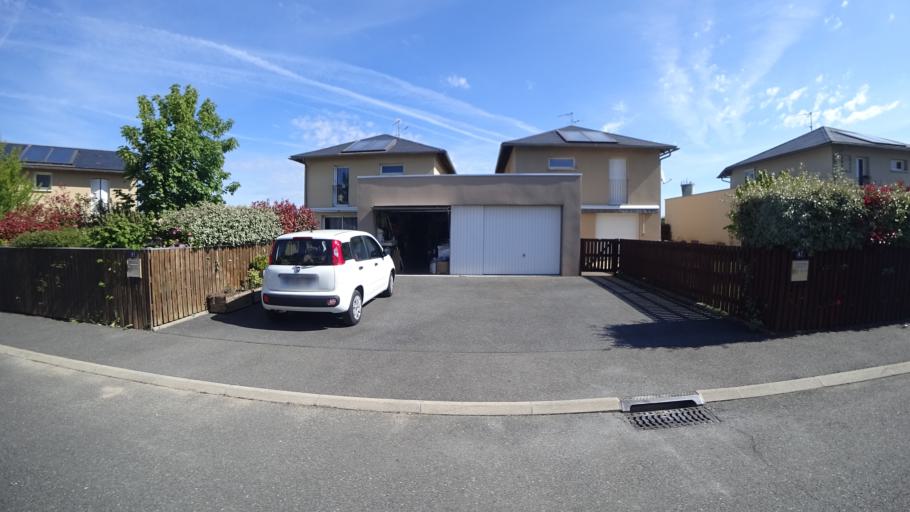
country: FR
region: Midi-Pyrenees
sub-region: Departement de l'Aveyron
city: Rodez
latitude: 44.3800
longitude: 2.5737
